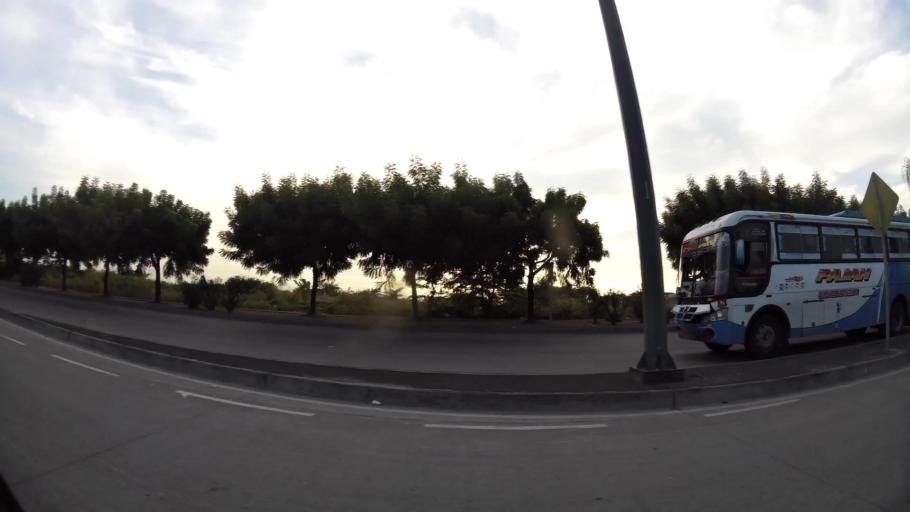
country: EC
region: Guayas
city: Eloy Alfaro
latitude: -2.1005
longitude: -79.8895
